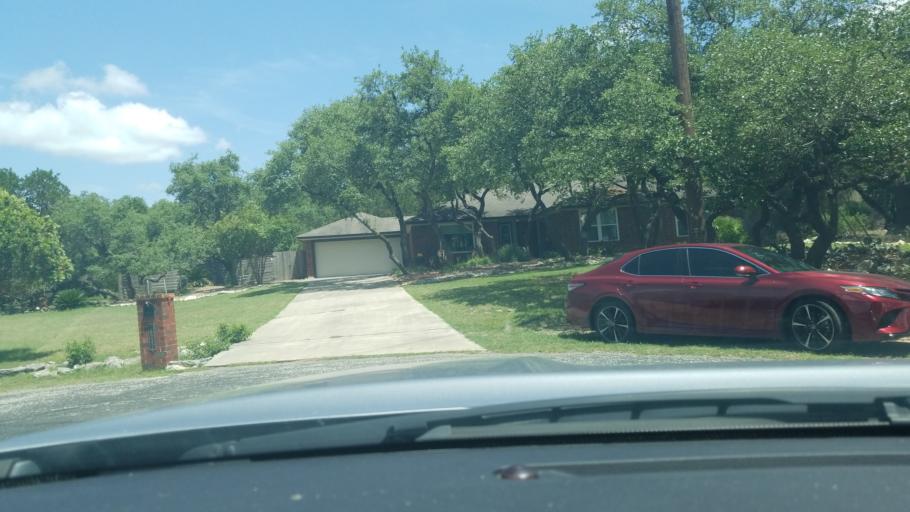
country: US
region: Texas
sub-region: Bexar County
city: Timberwood Park
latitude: 29.6903
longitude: -98.4870
